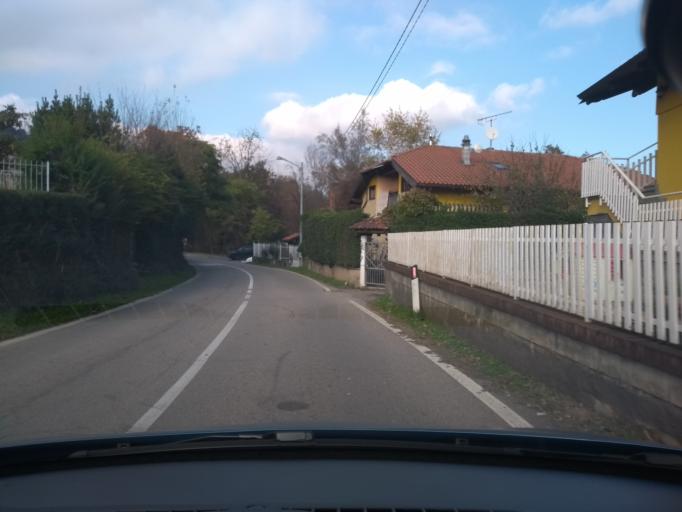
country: IT
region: Piedmont
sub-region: Provincia di Torino
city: La Cassa
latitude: 45.1836
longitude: 7.5162
